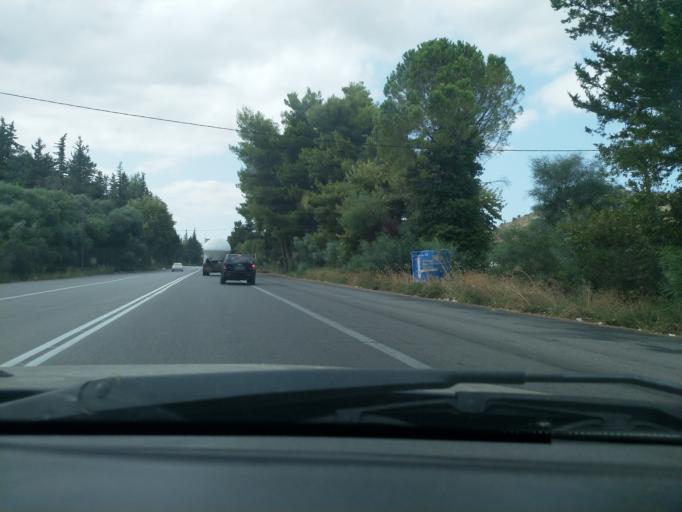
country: GR
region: Crete
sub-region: Nomos Chanias
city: Georgioupolis
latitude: 35.3655
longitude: 24.2190
